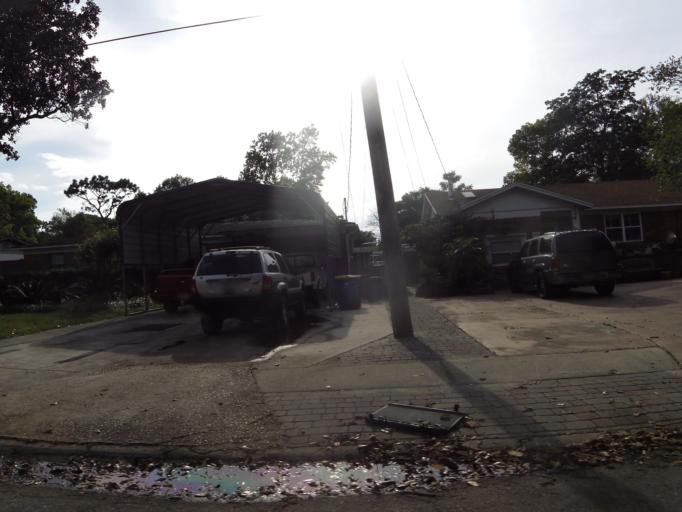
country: US
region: Florida
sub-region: Duval County
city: Jacksonville
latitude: 30.3407
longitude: -81.5936
